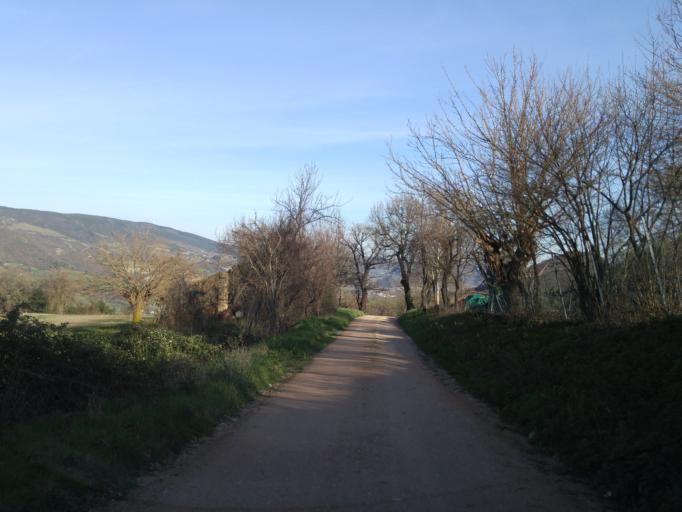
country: IT
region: The Marches
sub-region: Provincia di Pesaro e Urbino
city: Canavaccio
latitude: 43.6839
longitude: 12.6839
